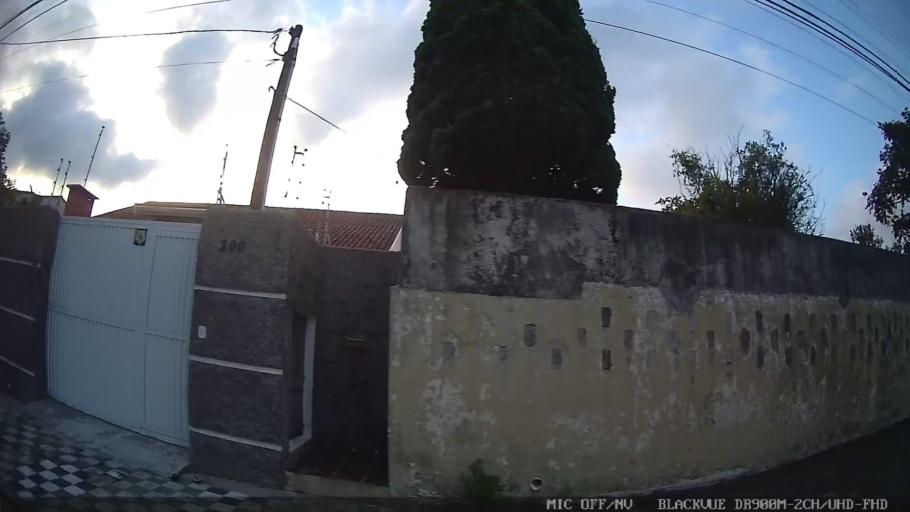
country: BR
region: Sao Paulo
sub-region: Peruibe
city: Peruibe
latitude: -24.3240
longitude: -47.0037
